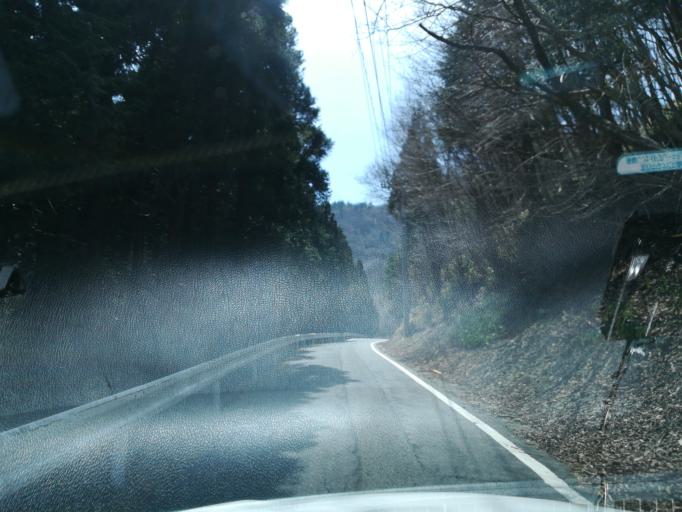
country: JP
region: Tokushima
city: Wakimachi
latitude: 33.8770
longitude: 134.0594
